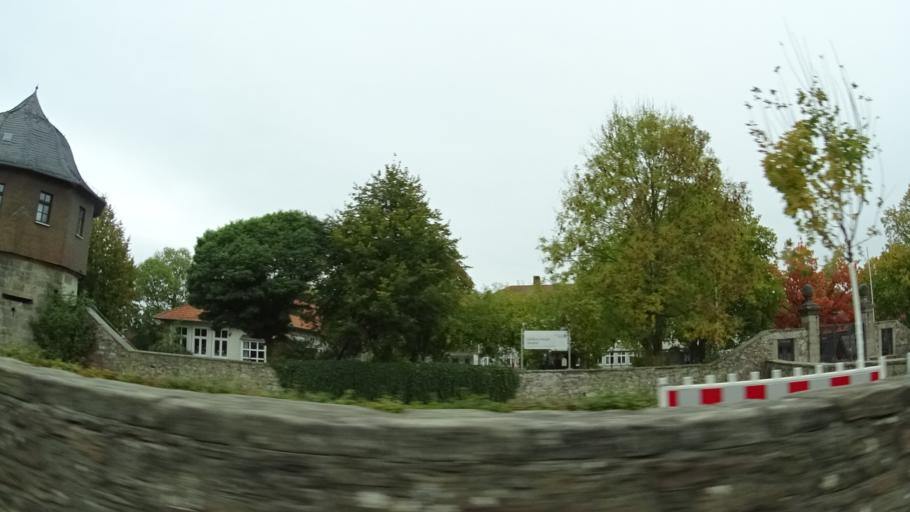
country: DE
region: Hesse
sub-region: Regierungsbezirk Kassel
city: Neuhof
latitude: 50.4535
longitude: 9.6153
